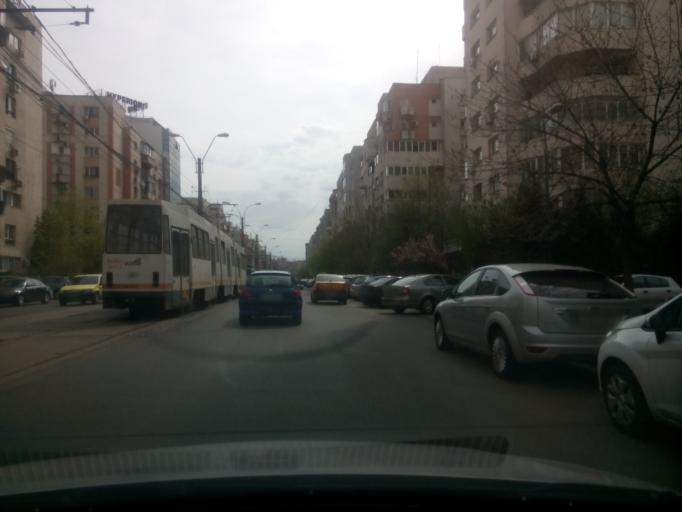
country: RO
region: Bucuresti
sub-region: Municipiul Bucuresti
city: Bucharest
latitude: 44.4326
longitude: 26.1240
